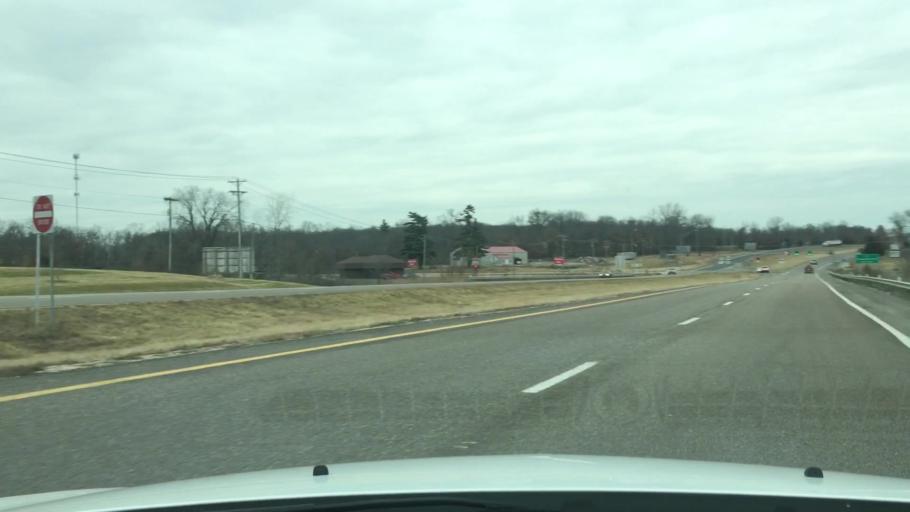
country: US
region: Missouri
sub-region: Callaway County
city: Fulton
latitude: 38.9465
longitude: -91.9408
